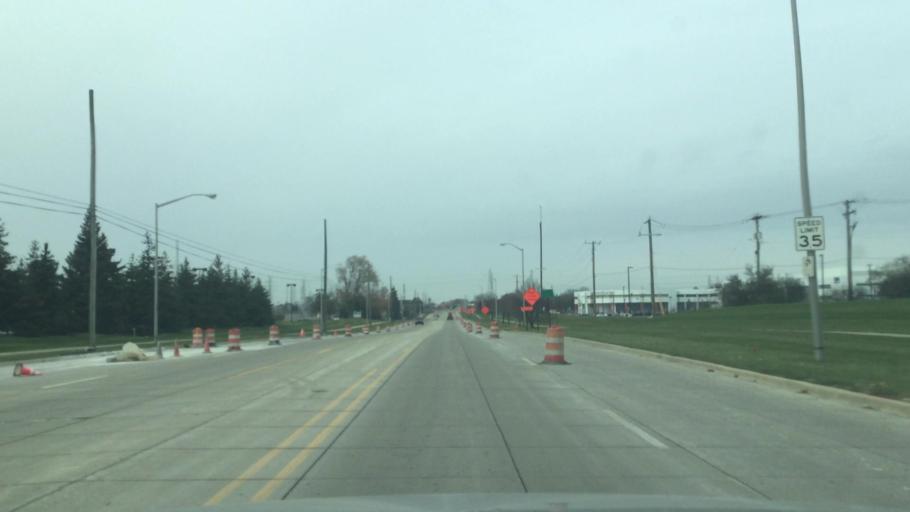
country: US
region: Michigan
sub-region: Oakland County
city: Pontiac
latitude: 42.6198
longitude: -83.2584
